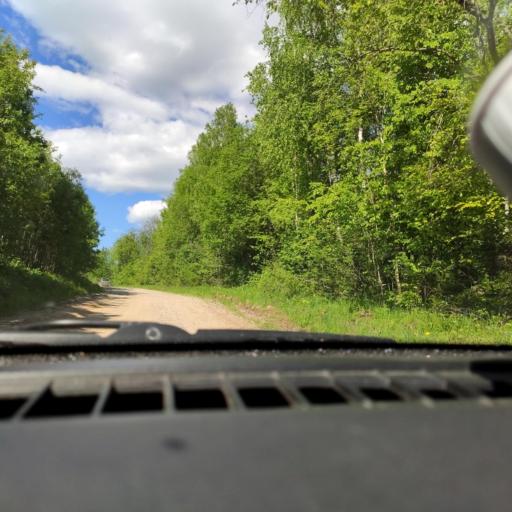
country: RU
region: Perm
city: Polazna
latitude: 58.2949
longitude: 56.1435
